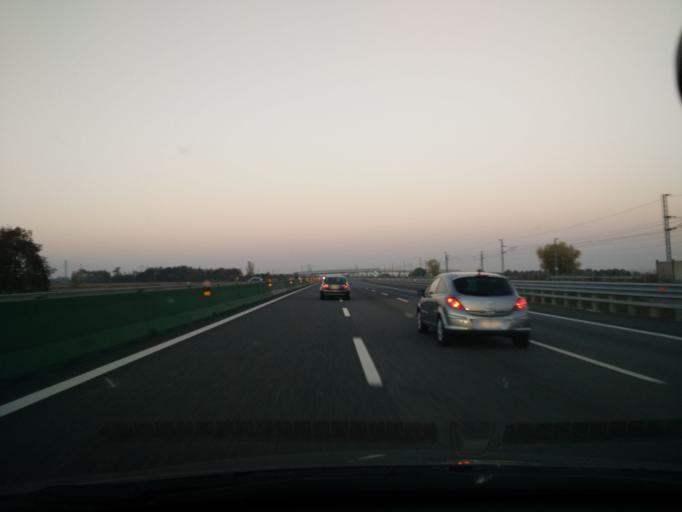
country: IT
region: Piedmont
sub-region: Provincia di Vercelli
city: Saluggia
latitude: 45.2706
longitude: 8.0178
